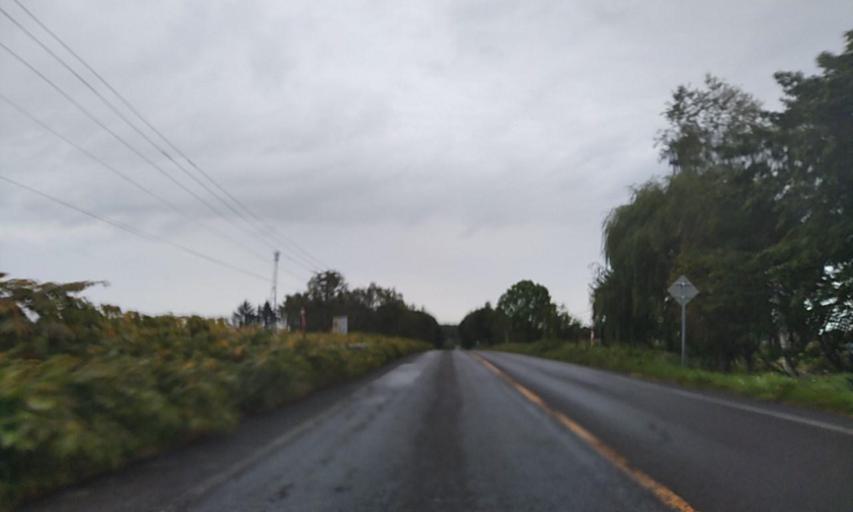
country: JP
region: Hokkaido
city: Mombetsu
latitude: 44.4825
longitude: 143.0988
